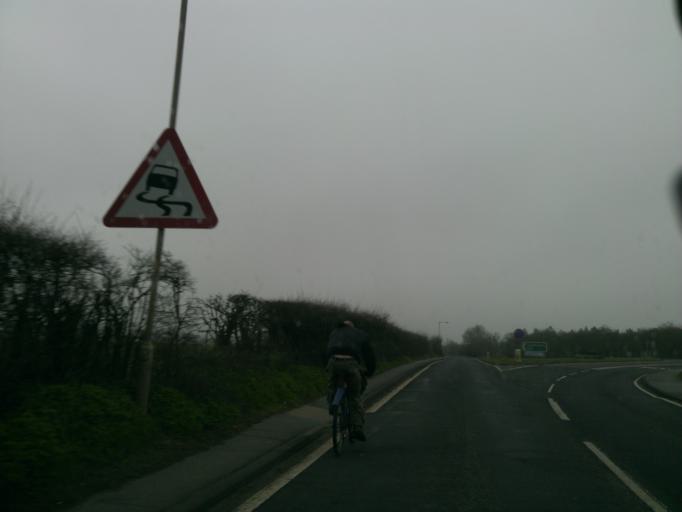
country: GB
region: England
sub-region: Essex
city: Kelvedon
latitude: 51.8469
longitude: 0.7210
